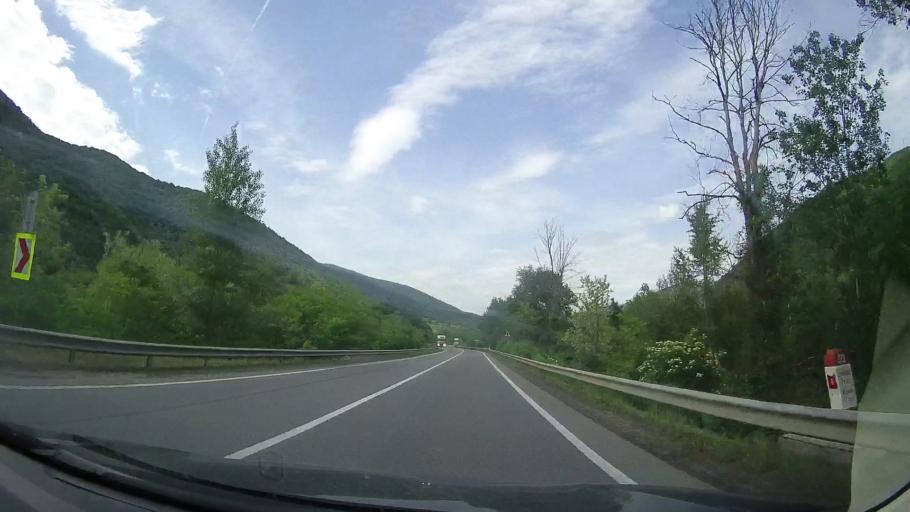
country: RO
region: Caras-Severin
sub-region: Oras Baile Herculane
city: Baile Herculane
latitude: 44.8431
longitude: 22.3829
